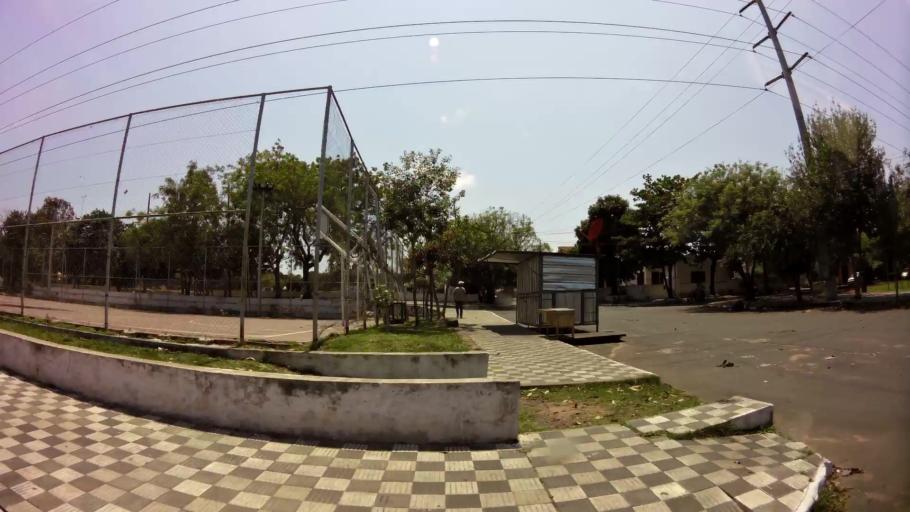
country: PY
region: Asuncion
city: Asuncion
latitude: -25.3043
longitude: -57.6495
